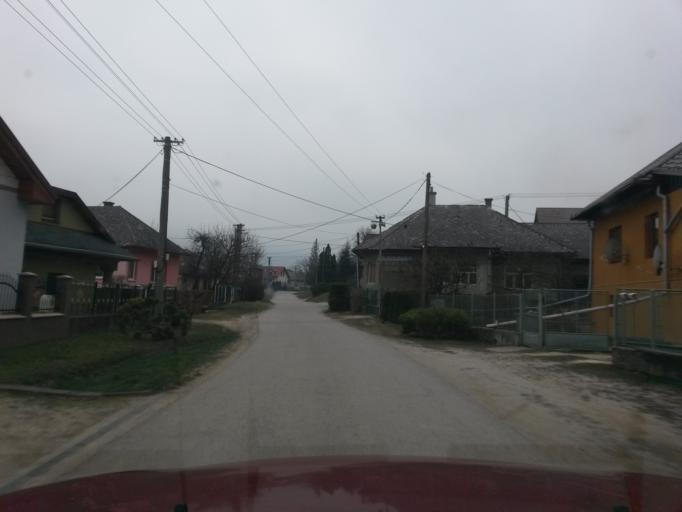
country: SK
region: Kosicky
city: Medzev
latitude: 48.6048
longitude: 20.7446
